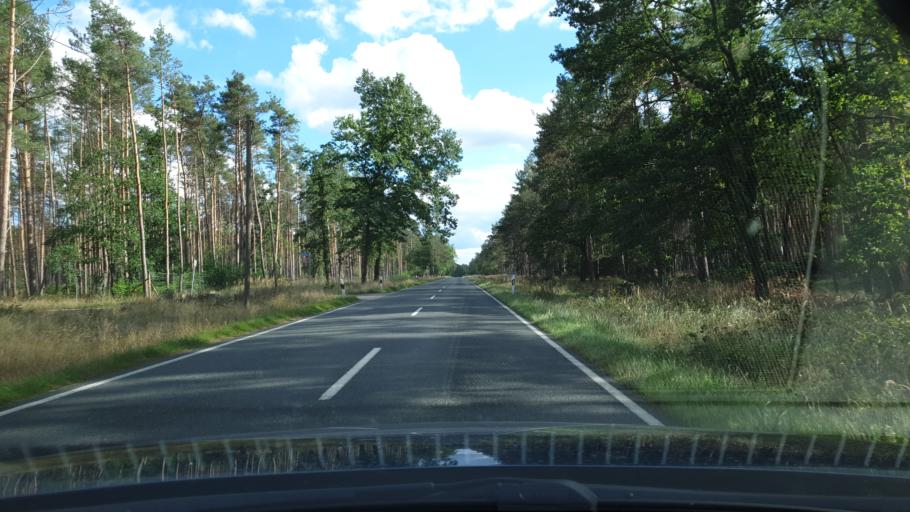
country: DE
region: Saxony-Anhalt
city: Radis
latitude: 51.7781
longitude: 12.4890
